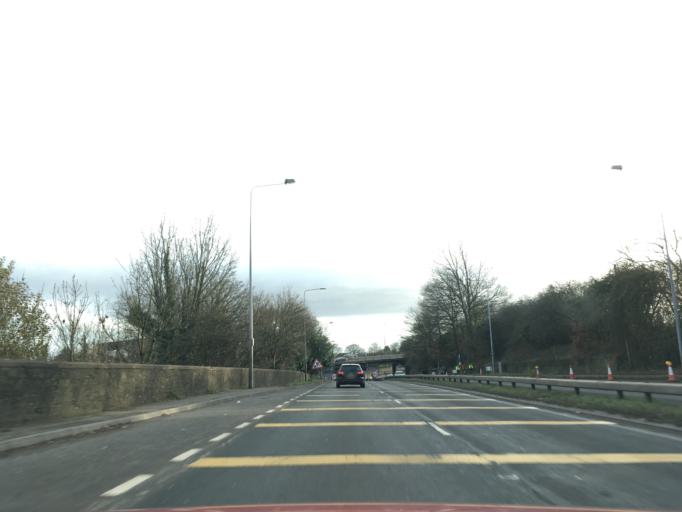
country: GB
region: Wales
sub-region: Newport
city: Newport
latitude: 51.5686
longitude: -3.0371
